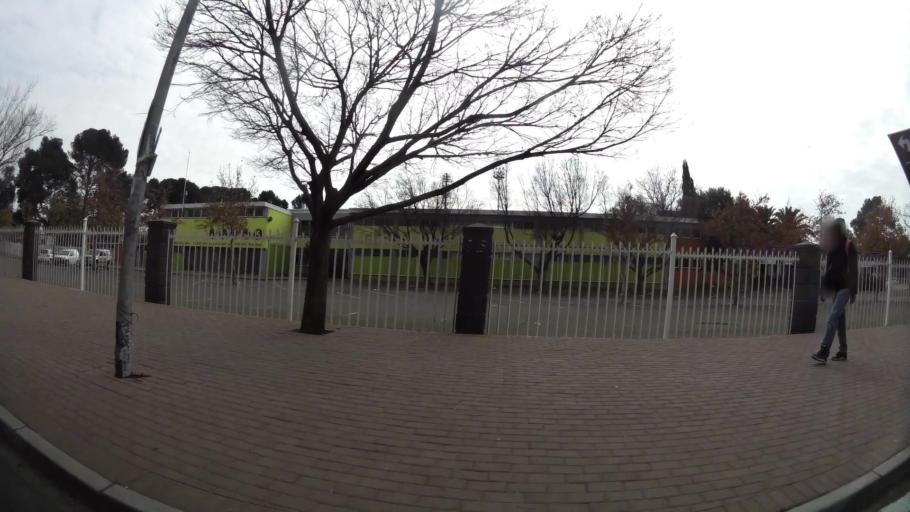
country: ZA
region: Orange Free State
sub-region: Mangaung Metropolitan Municipality
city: Bloemfontein
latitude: -29.1202
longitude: 26.2087
